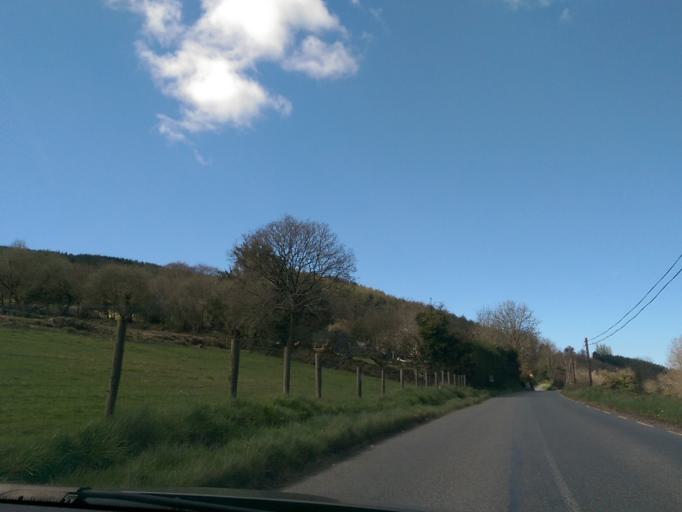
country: IE
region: Leinster
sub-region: Wicklow
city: Carnew
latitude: 52.8074
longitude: -6.4829
